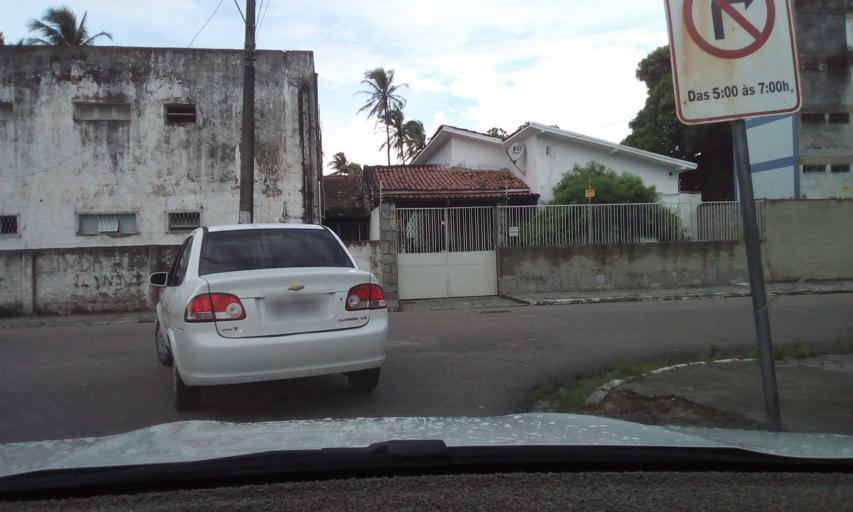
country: BR
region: Paraiba
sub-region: Joao Pessoa
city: Joao Pessoa
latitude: -7.1382
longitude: -34.8859
